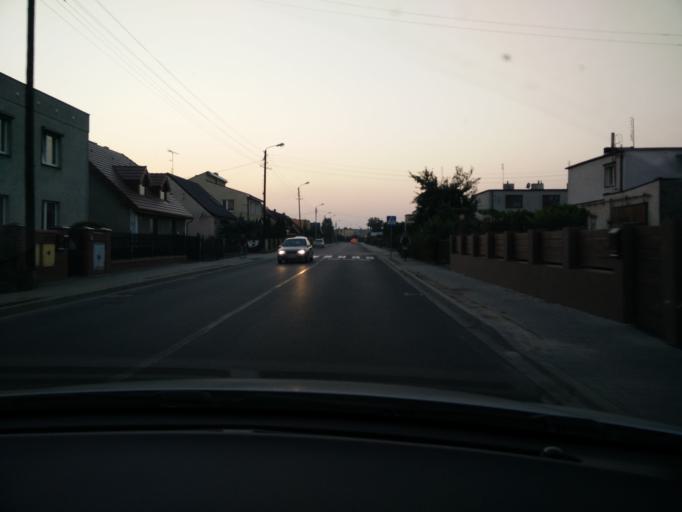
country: PL
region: Greater Poland Voivodeship
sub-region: Powiat sredzki
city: Sroda Wielkopolska
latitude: 52.2310
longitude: 17.2601
